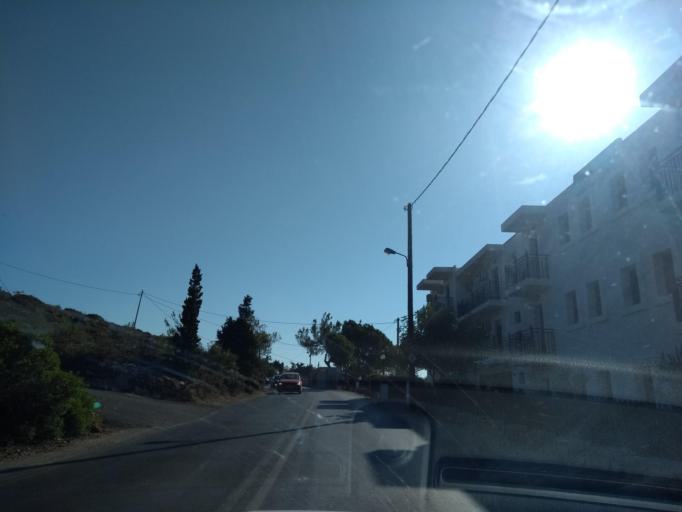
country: GR
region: Crete
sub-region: Nomos Chanias
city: Pithari
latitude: 35.5523
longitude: 24.0854
